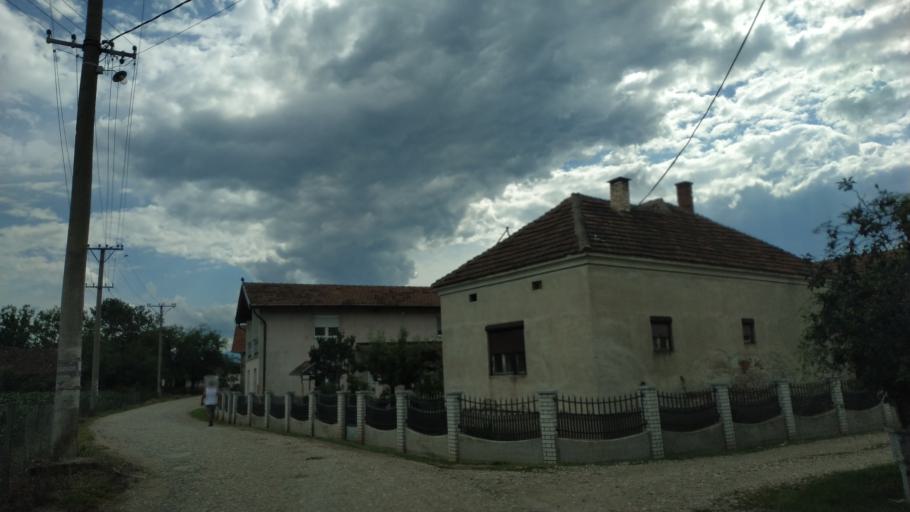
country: RS
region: Central Serbia
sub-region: Nisavski Okrug
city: Razanj
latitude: 43.5920
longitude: 21.6081
